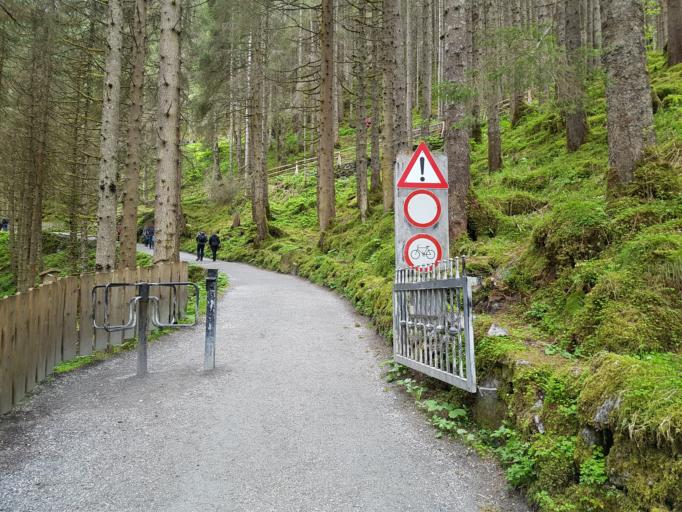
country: AT
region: Salzburg
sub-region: Politischer Bezirk Zell am See
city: Krimml
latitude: 47.2092
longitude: 12.1682
